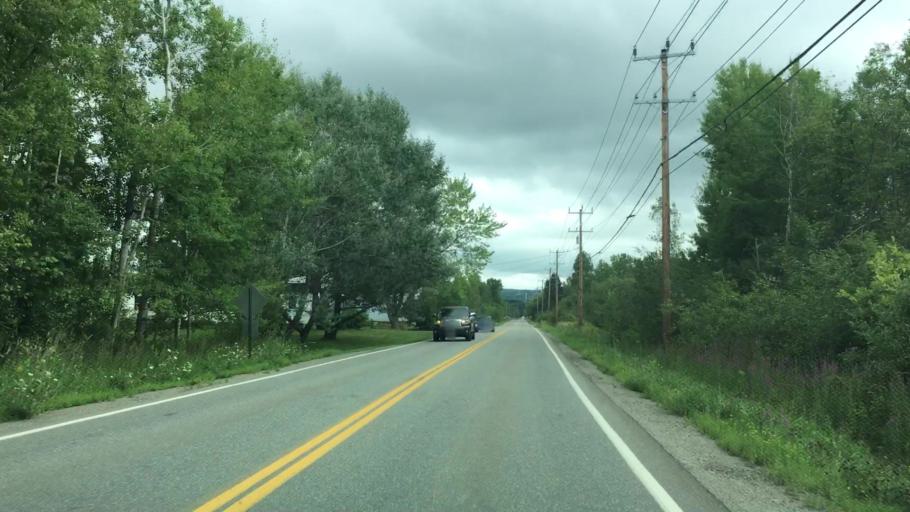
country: US
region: Maine
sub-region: Penobscot County
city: Brewer
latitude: 44.7672
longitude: -68.7556
